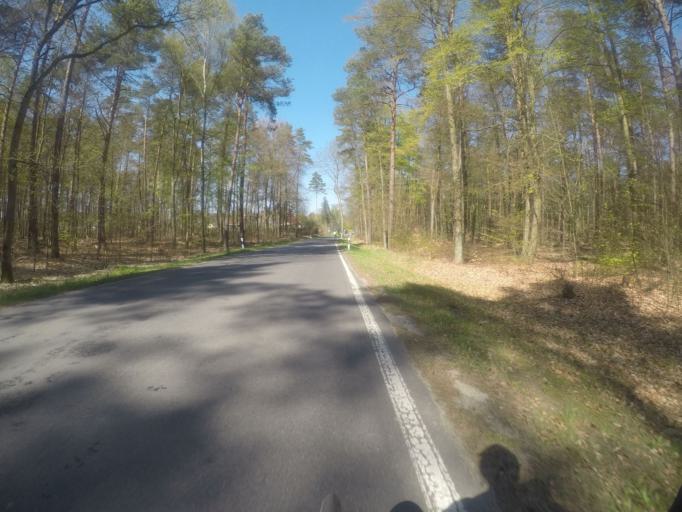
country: DE
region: Brandenburg
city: Rudnitz
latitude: 52.7518
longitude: 13.5664
